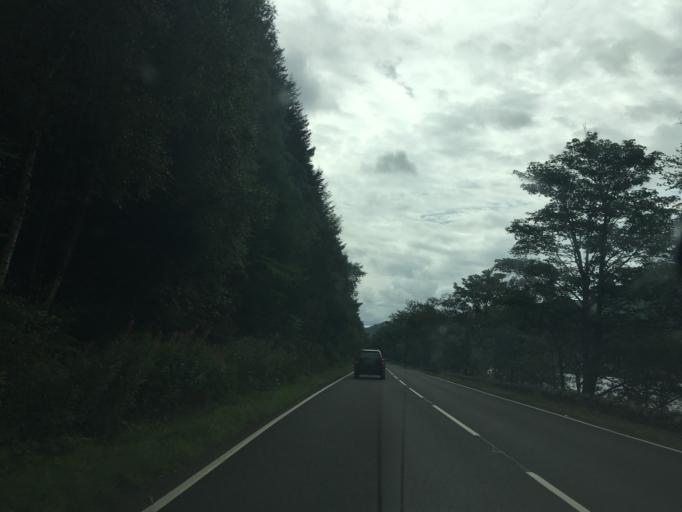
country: GB
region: Scotland
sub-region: Stirling
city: Callander
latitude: 56.2814
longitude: -4.2838
